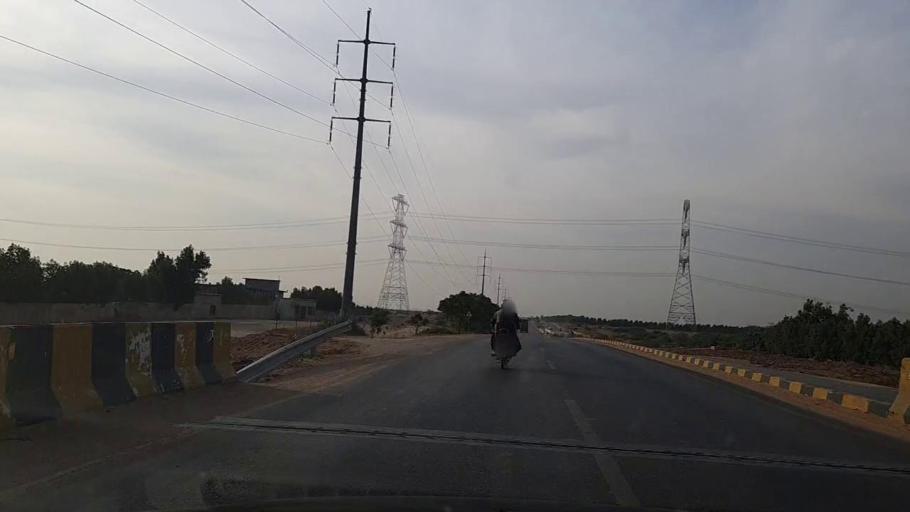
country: PK
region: Sindh
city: Gharo
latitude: 24.8183
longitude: 67.4883
